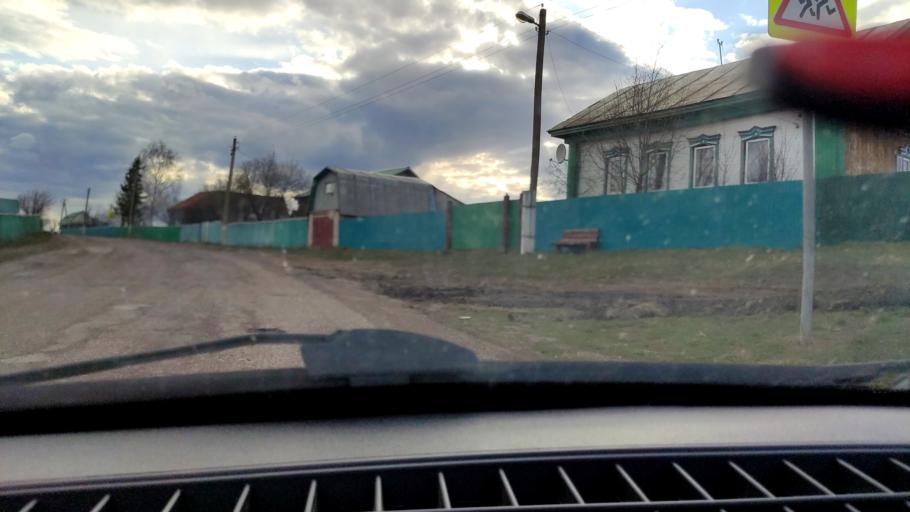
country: RU
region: Bashkortostan
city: Karmaskaly
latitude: 54.3358
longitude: 56.0041
